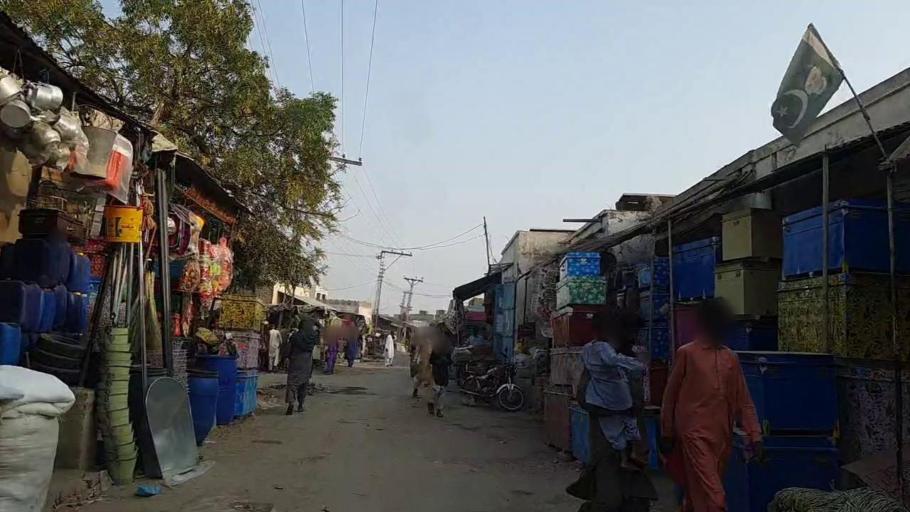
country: PK
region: Sindh
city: Naukot
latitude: 24.6570
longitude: 69.2901
